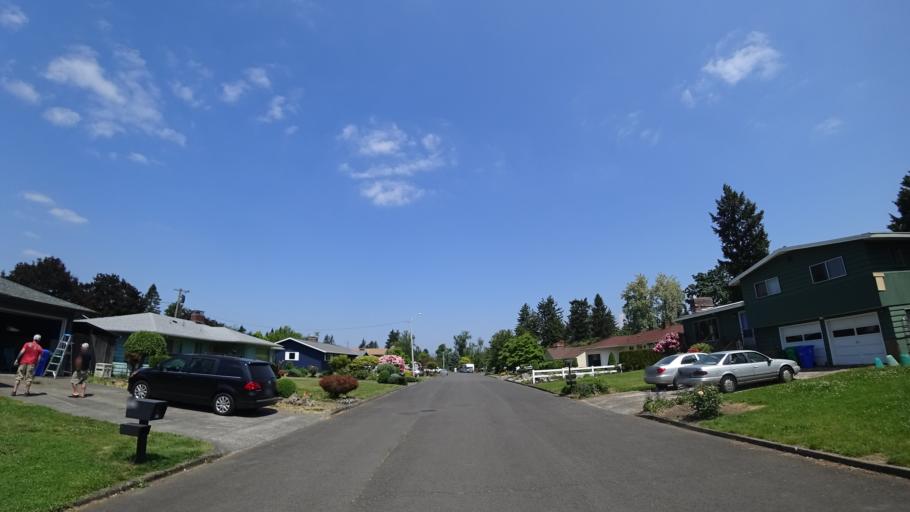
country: US
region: Oregon
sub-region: Multnomah County
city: Fairview
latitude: 45.5281
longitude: -122.5052
